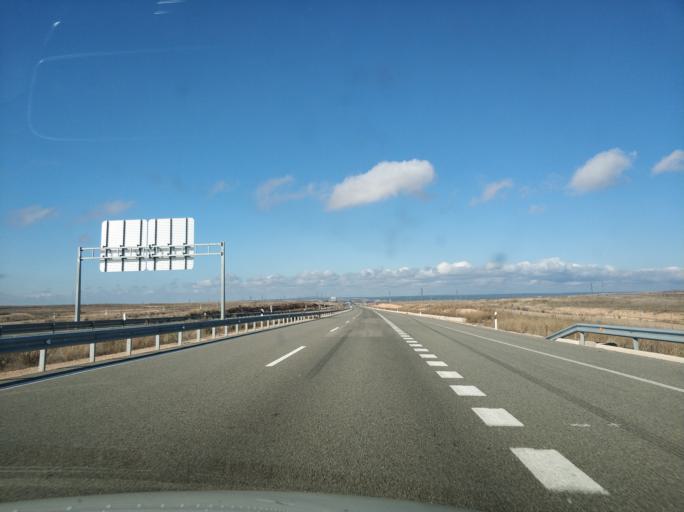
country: ES
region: Castille and Leon
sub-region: Provincia de Soria
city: Coscurita
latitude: 41.4234
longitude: -2.4909
